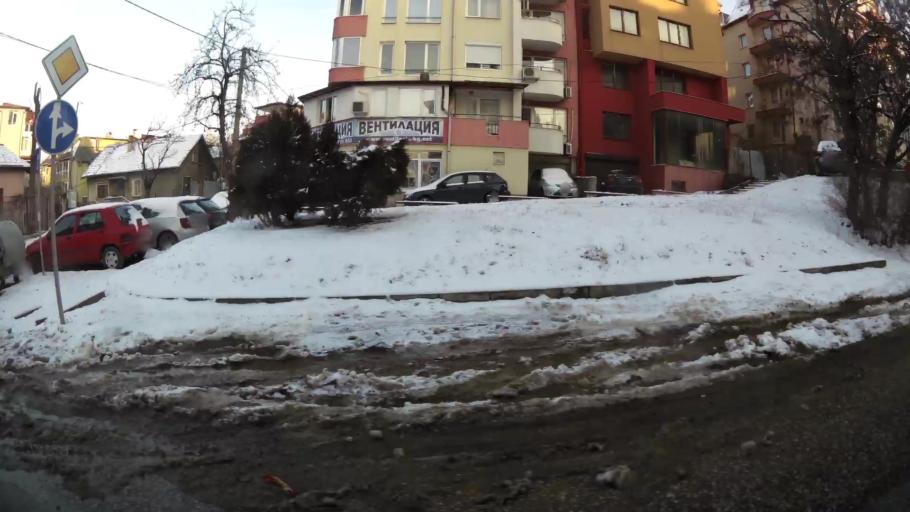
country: BG
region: Sofia-Capital
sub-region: Stolichna Obshtina
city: Sofia
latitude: 42.6955
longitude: 23.3607
